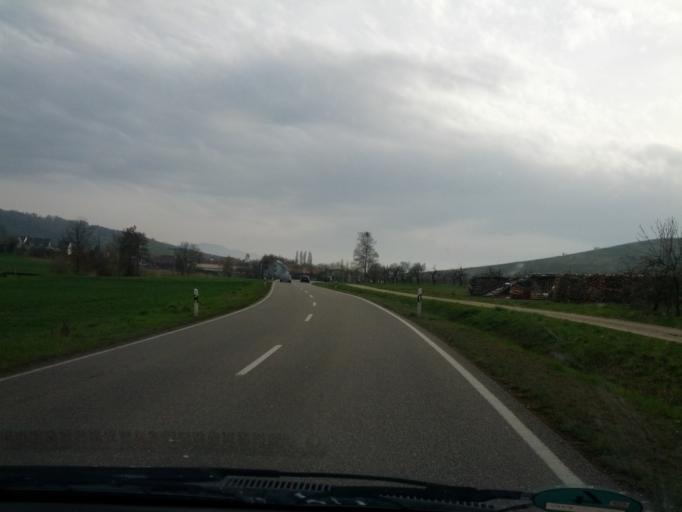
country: DE
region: Baden-Wuerttemberg
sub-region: Freiburg Region
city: Schallstadt
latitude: 47.9477
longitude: 7.7577
